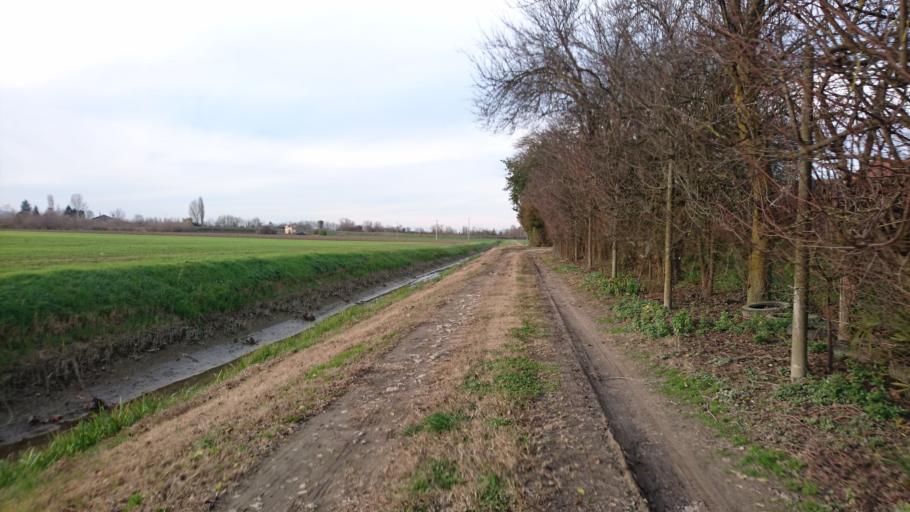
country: IT
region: Veneto
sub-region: Provincia di Padova
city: Polverara
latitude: 45.3243
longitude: 11.9494
